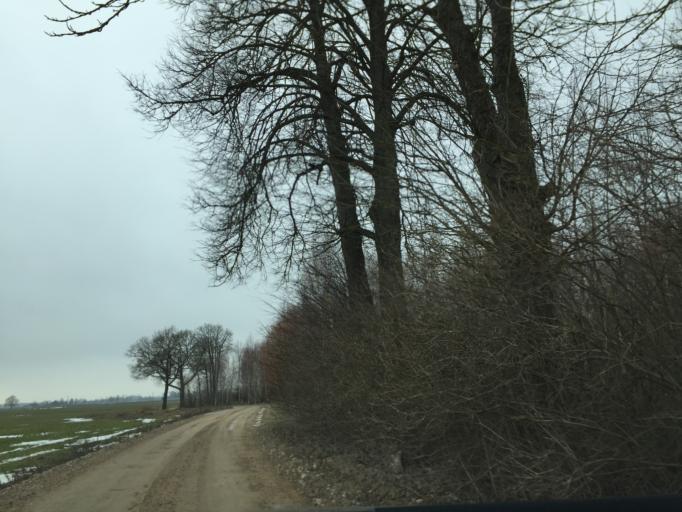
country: LV
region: Rundales
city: Pilsrundale
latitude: 56.5628
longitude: 24.0435
